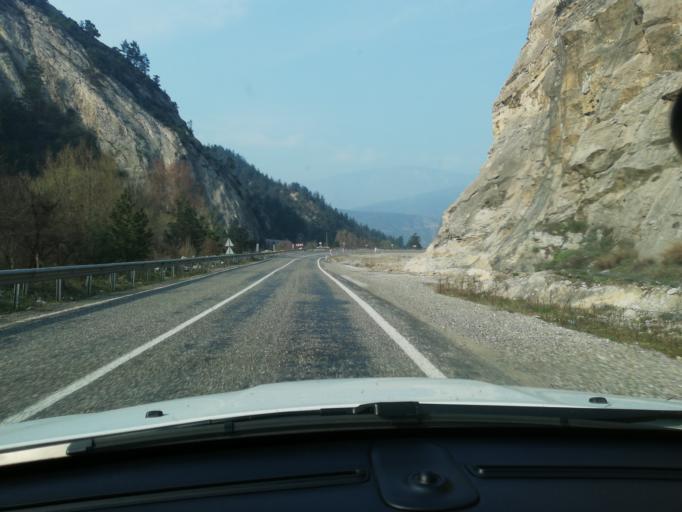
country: TR
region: Karabuk
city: Karabuk
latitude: 41.1594
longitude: 32.5525
